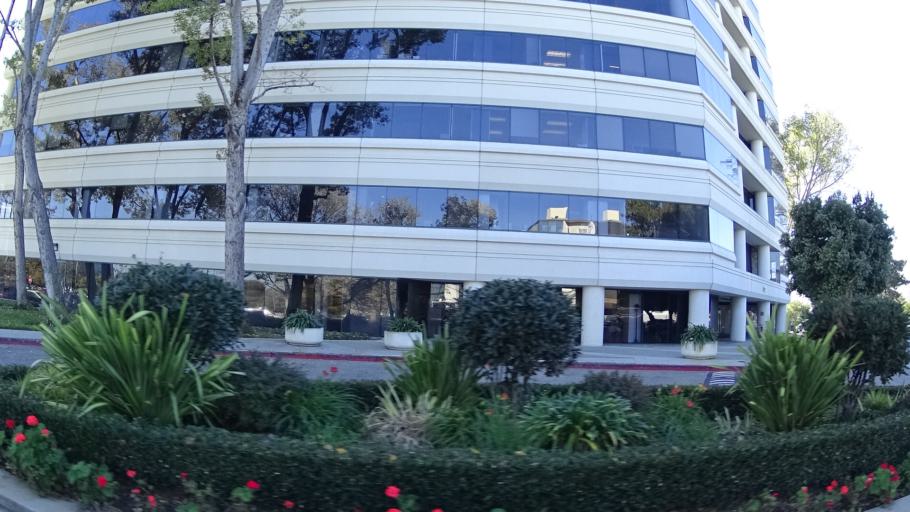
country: US
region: California
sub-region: San Mateo County
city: Burlingame
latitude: 37.5892
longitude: -122.3411
